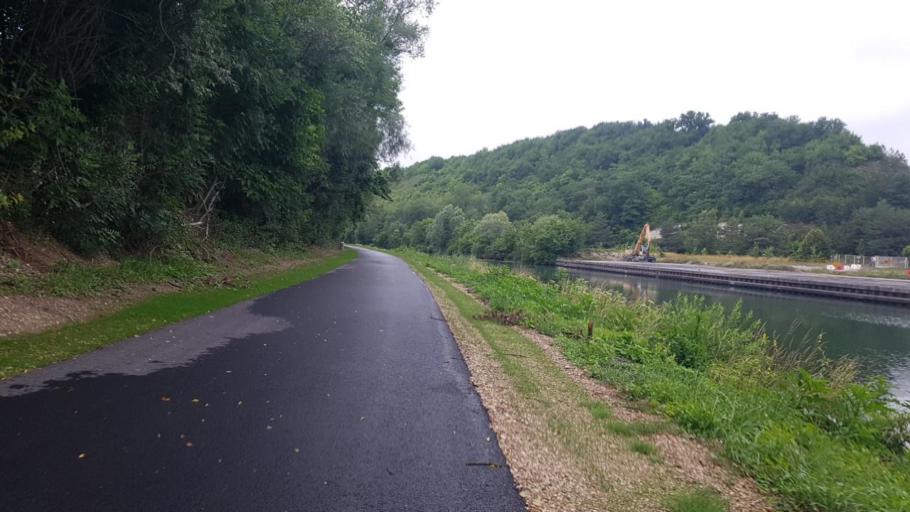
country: FR
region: Champagne-Ardenne
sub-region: Departement de la Marne
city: Vitry-le-Francois
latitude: 48.7675
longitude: 4.5583
